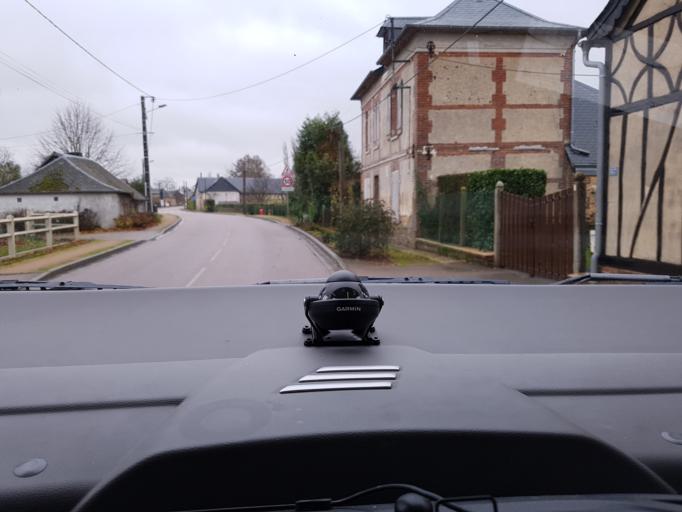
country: FR
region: Haute-Normandie
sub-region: Departement de l'Eure
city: Pont-Saint-Pierre
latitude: 49.3145
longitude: 1.3065
